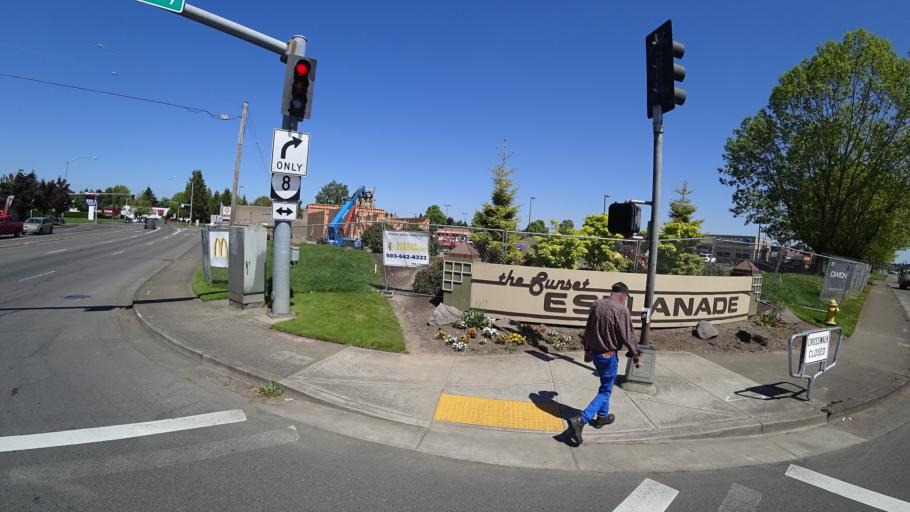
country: US
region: Oregon
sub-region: Washington County
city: Hillsboro
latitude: 45.5068
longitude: -122.9609
